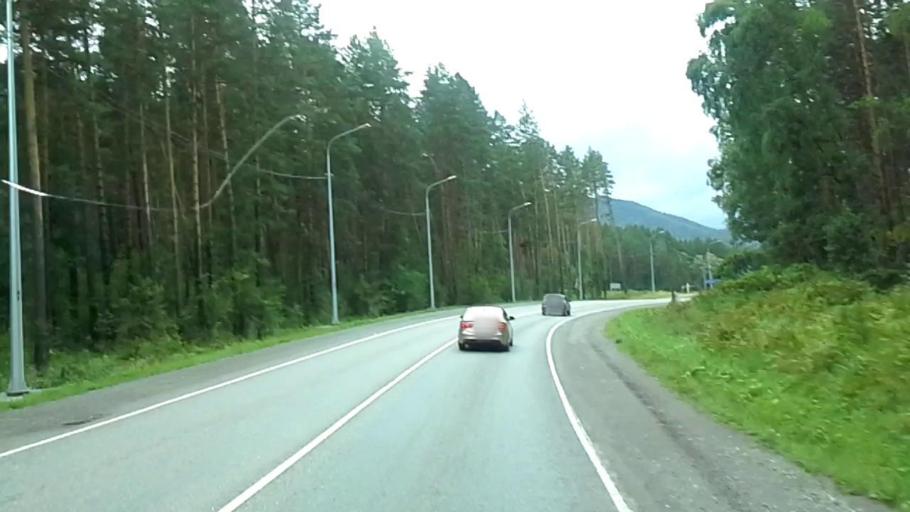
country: RU
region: Altay
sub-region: Mayminskiy Rayon
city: Manzherok
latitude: 51.8236
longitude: 85.7894
